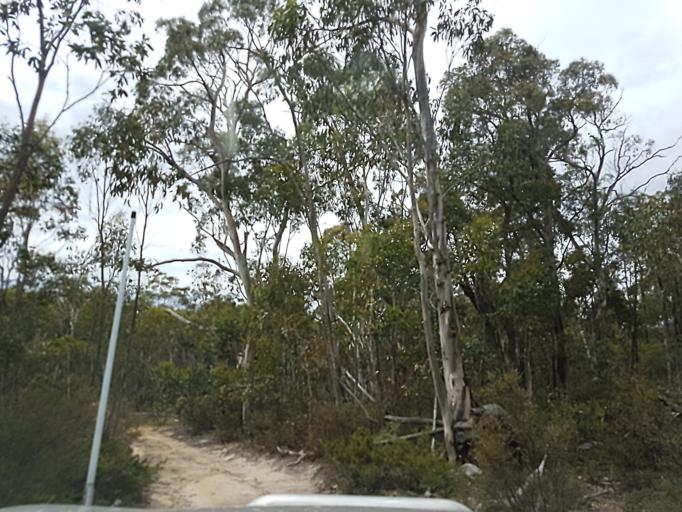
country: AU
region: New South Wales
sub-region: Snowy River
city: Jindabyne
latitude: -36.8292
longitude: 148.2239
